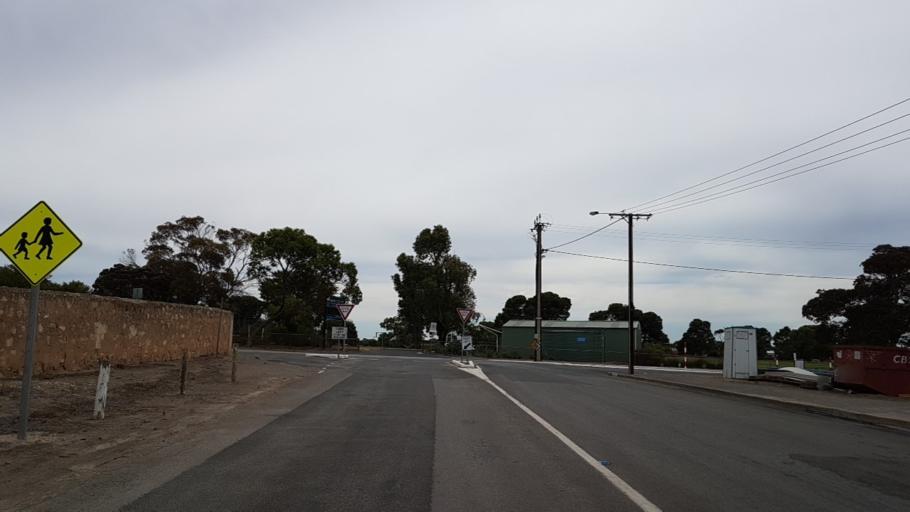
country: AU
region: South Australia
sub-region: Yorke Peninsula
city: Port Victoria
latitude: -34.7674
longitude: 137.5939
